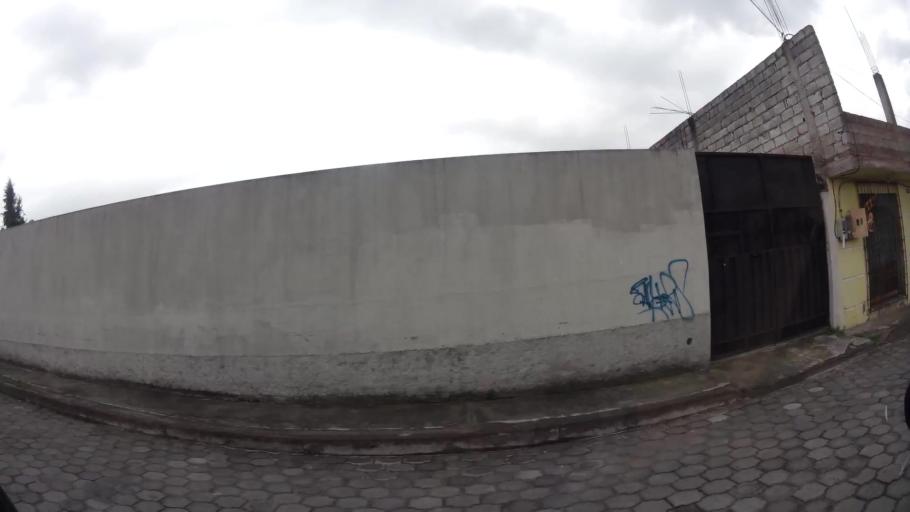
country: EC
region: Pichincha
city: Sangolqui
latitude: -0.3223
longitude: -78.4688
